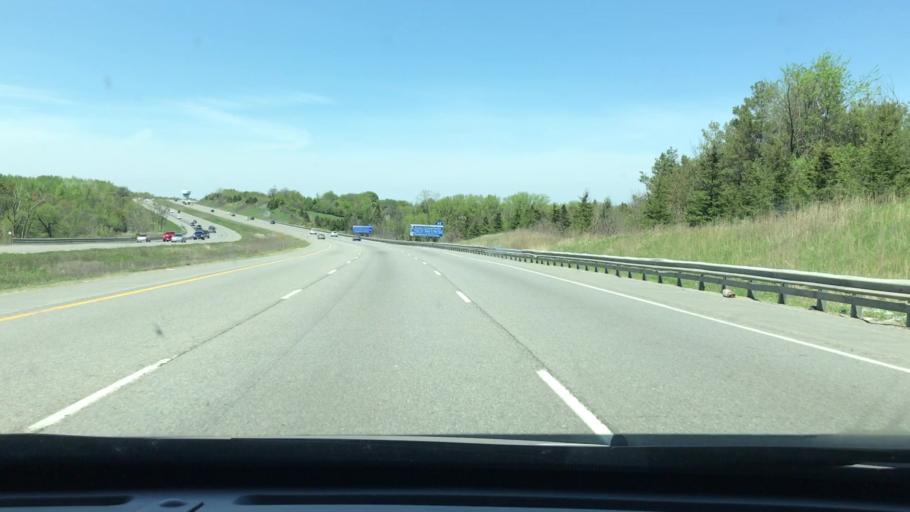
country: CA
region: Ontario
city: Newmarket
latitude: 43.9965
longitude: -79.3964
